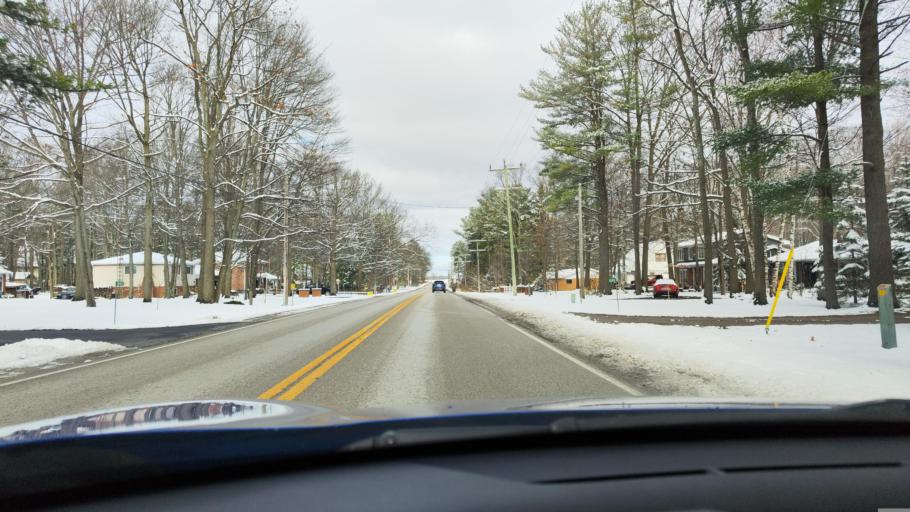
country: CA
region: Ontario
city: Barrie
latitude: 44.3854
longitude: -79.7584
